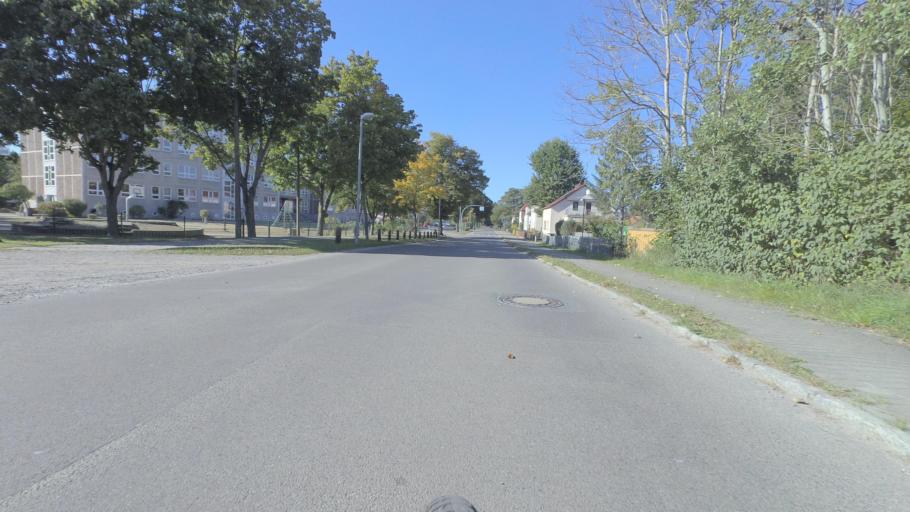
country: DE
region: Brandenburg
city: Sperenberg
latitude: 52.1408
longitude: 13.3599
